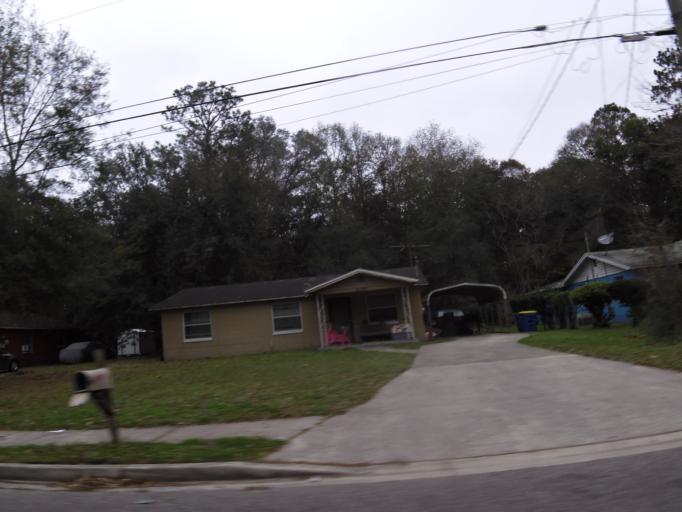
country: US
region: Florida
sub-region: Duval County
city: Jacksonville
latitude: 30.3777
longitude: -81.6967
